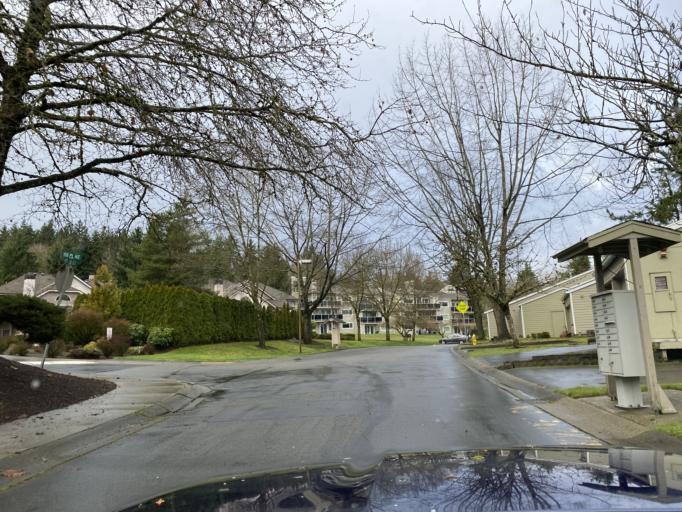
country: US
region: Washington
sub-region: King County
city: Redmond
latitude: 47.6675
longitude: -122.1314
